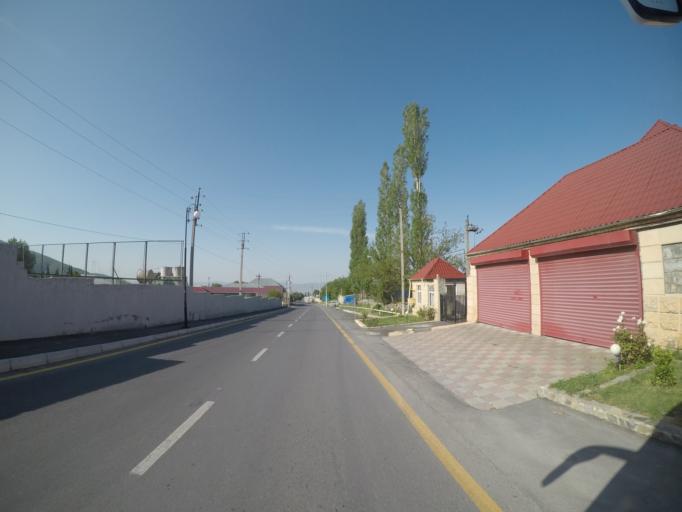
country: AZ
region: Shaki City
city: Sheki
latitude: 41.2180
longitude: 47.1692
